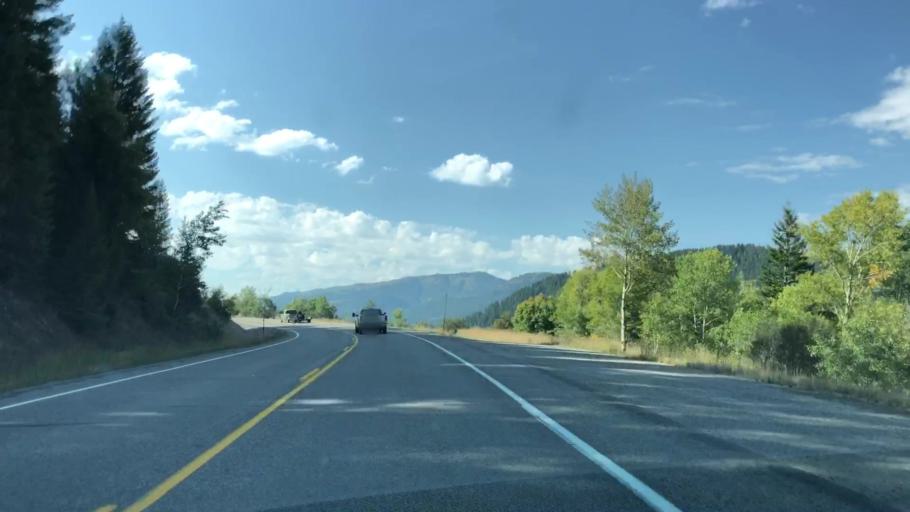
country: US
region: Idaho
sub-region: Teton County
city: Victor
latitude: 43.3156
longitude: -111.1461
